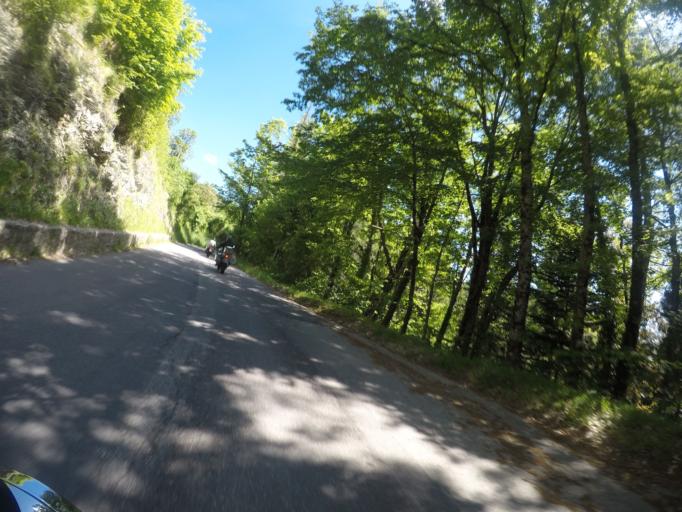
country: IT
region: Tuscany
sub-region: Provincia di Lucca
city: Careggine
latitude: 44.0993
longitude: 10.3282
